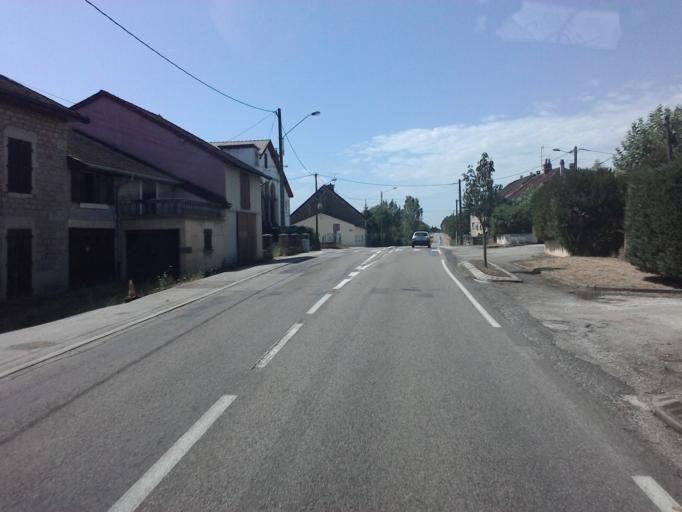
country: FR
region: Franche-Comte
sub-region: Departement du Jura
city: Montmorot
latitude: 46.6407
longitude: 5.5006
